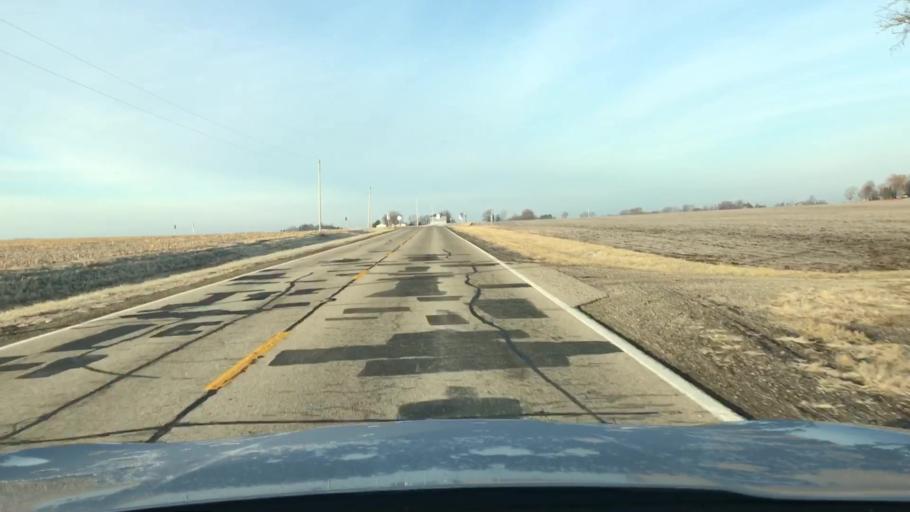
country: US
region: Illinois
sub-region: McLean County
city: Hudson
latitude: 40.6276
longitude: -88.9433
